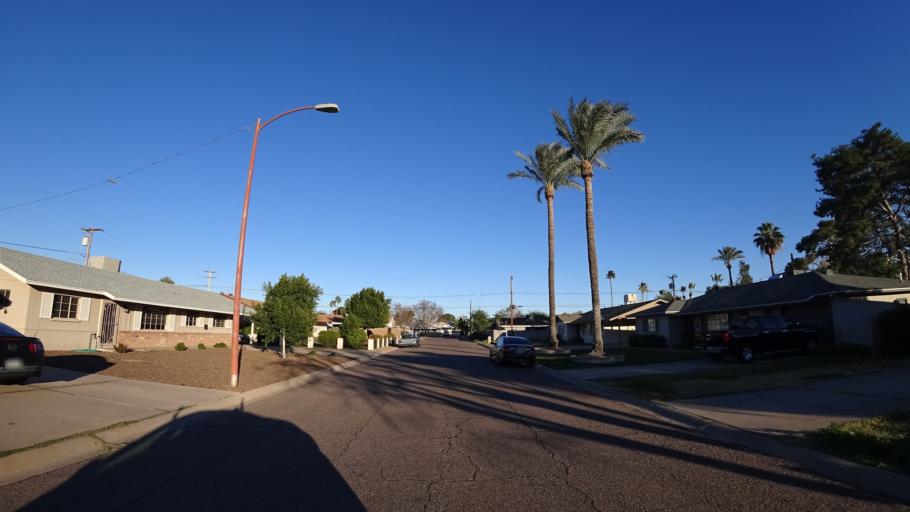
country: US
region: Arizona
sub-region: Maricopa County
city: Phoenix
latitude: 33.4853
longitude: -112.0375
